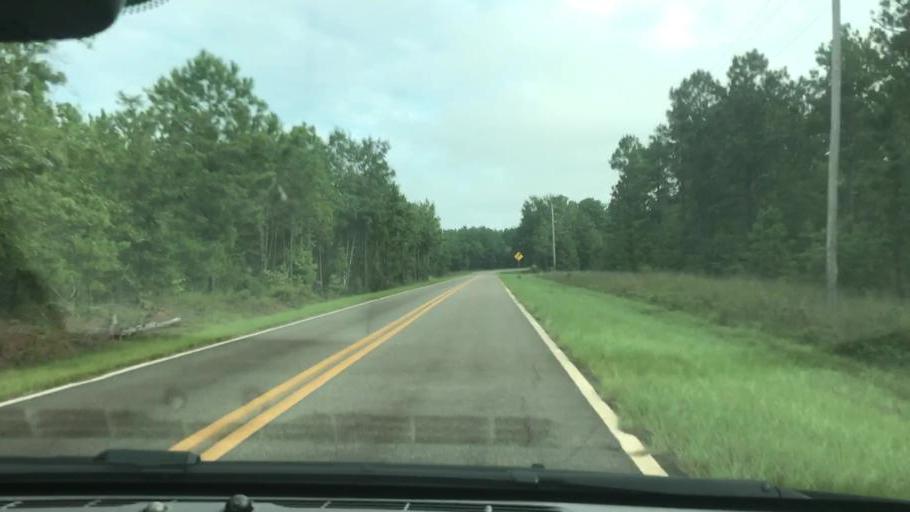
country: US
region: Georgia
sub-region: Stewart County
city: Lumpkin
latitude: 32.0400
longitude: -84.9094
